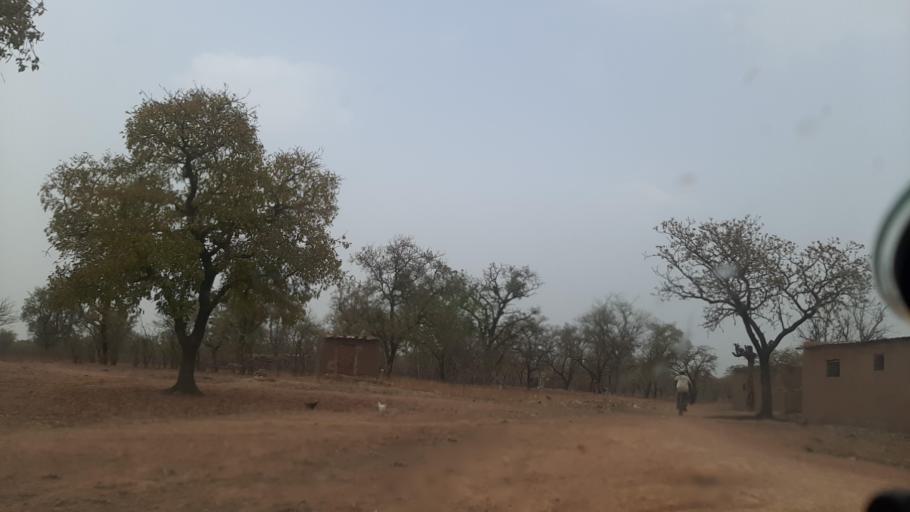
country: BF
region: Boucle du Mouhoun
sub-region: Province des Banwa
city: Salanso
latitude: 11.8693
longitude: -4.4474
